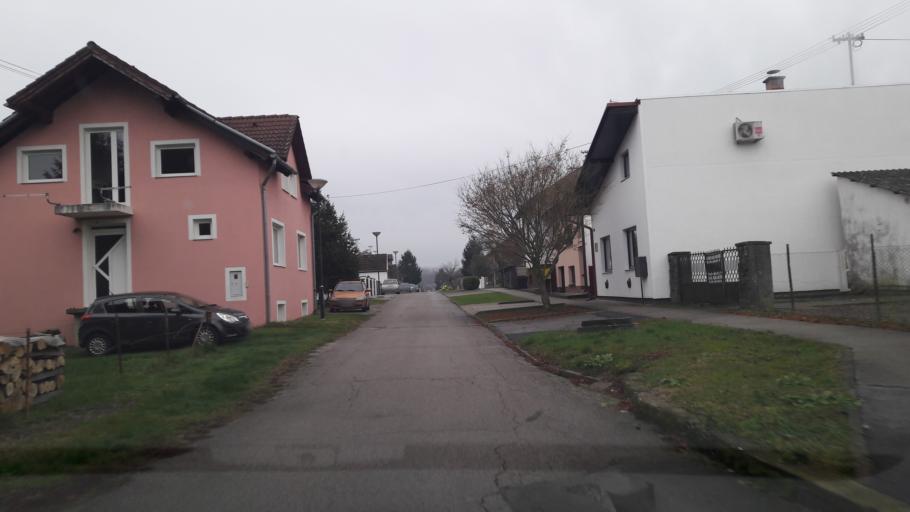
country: HR
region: Osjecko-Baranjska
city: Visnjevac
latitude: 45.5721
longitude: 18.6158
